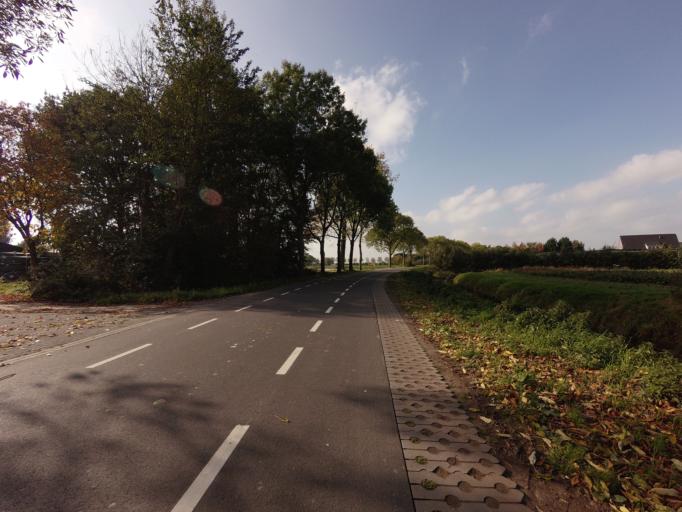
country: NL
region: Gelderland
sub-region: Gemeente Geldermalsen
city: Geldermalsen
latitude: 51.9114
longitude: 5.3141
